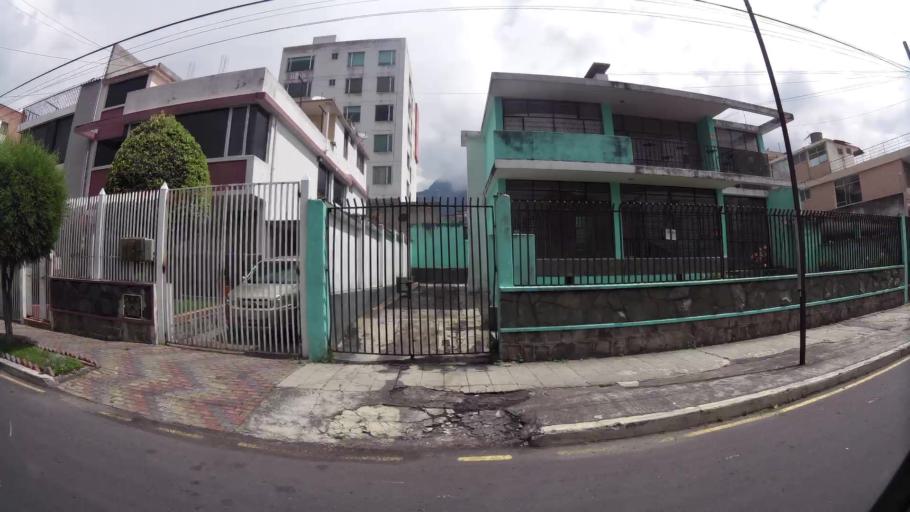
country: EC
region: Pichincha
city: Quito
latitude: -0.1887
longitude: -78.4937
